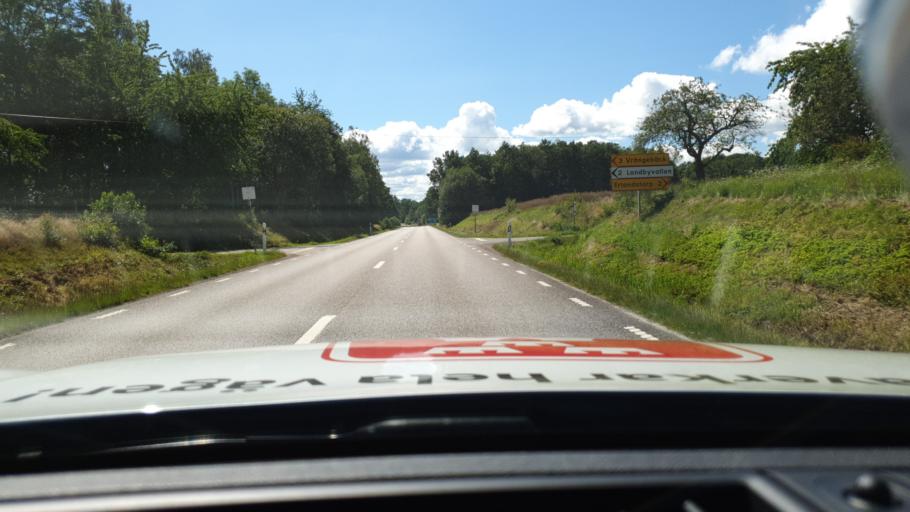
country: SE
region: Vaestra Goetaland
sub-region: Hjo Kommun
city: Hjo
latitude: 58.2312
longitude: 14.2168
